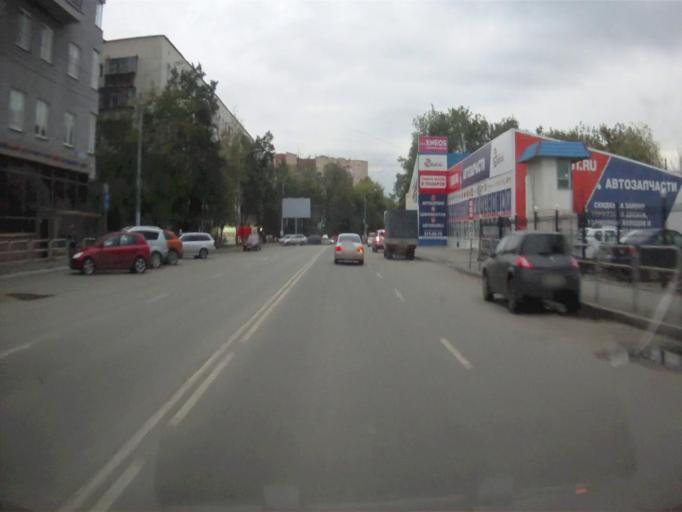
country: RU
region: Chelyabinsk
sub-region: Gorod Chelyabinsk
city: Chelyabinsk
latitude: 55.1527
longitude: 61.3984
